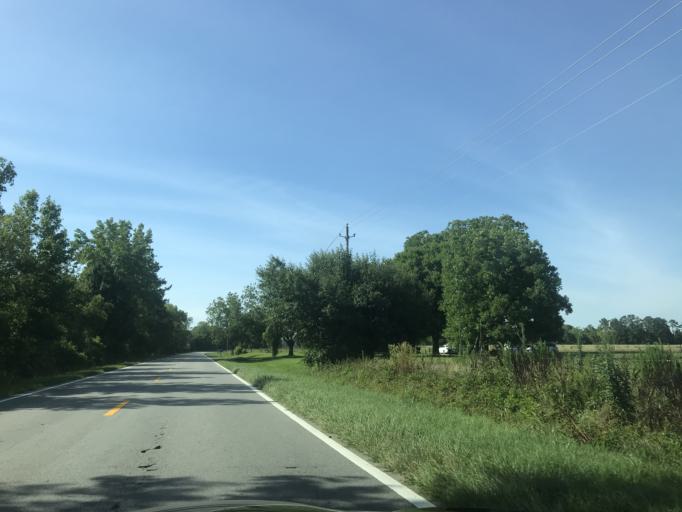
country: US
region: North Carolina
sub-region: Johnston County
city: Clayton
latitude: 35.6090
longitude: -78.5346
